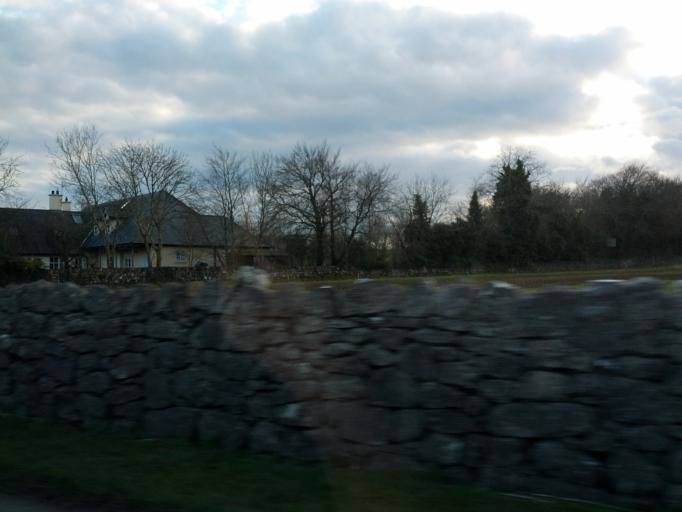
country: IE
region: Connaught
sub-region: County Galway
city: Athenry
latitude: 53.4063
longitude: -8.6884
